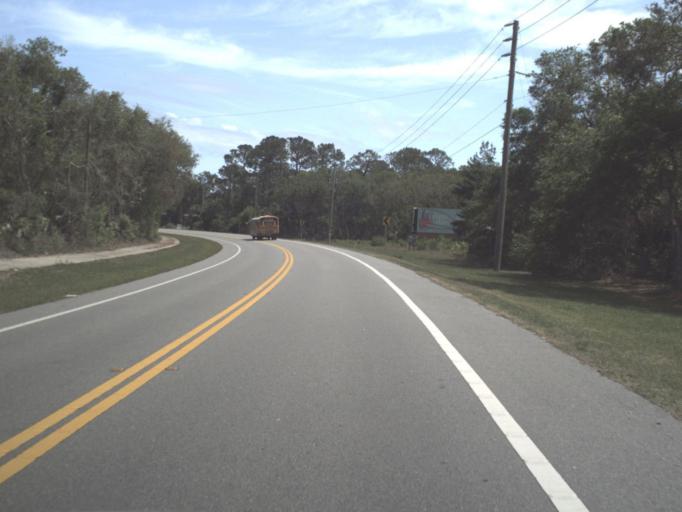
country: US
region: Florida
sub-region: Flagler County
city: Palm Coast
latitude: 29.5648
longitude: -81.1809
